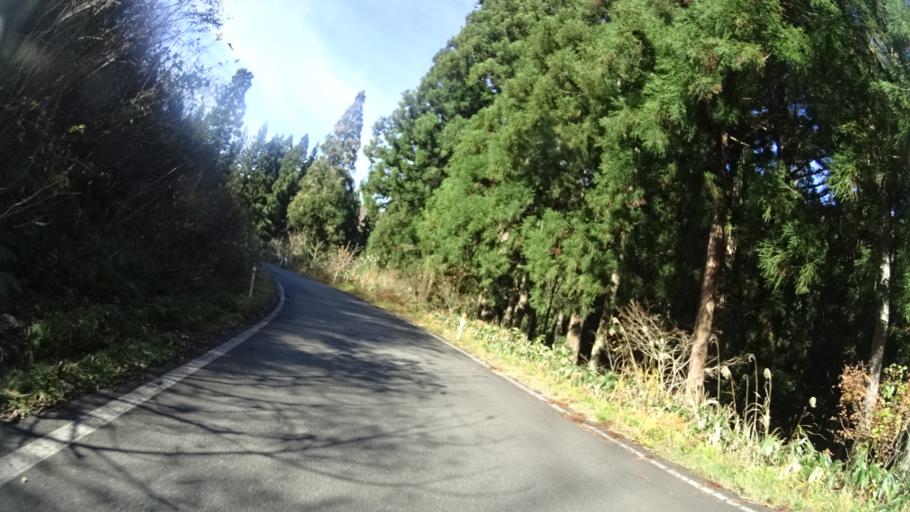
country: JP
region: Niigata
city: Muikamachi
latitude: 37.1782
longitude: 139.0869
